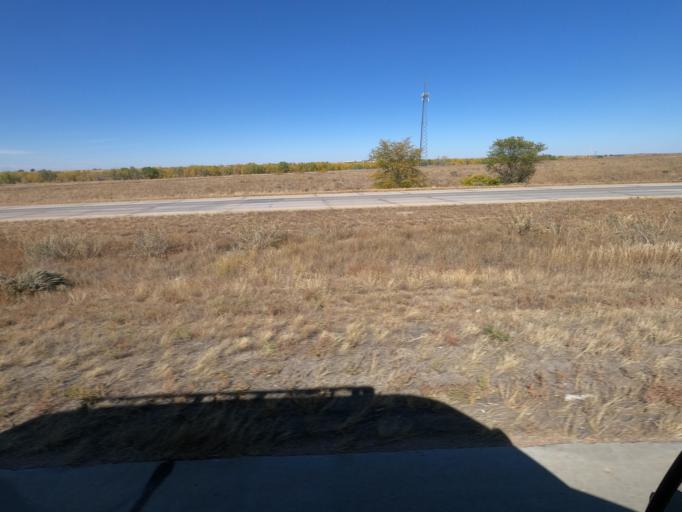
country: US
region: Colorado
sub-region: Morgan County
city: Fort Morgan
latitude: 40.2426
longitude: -103.9259
